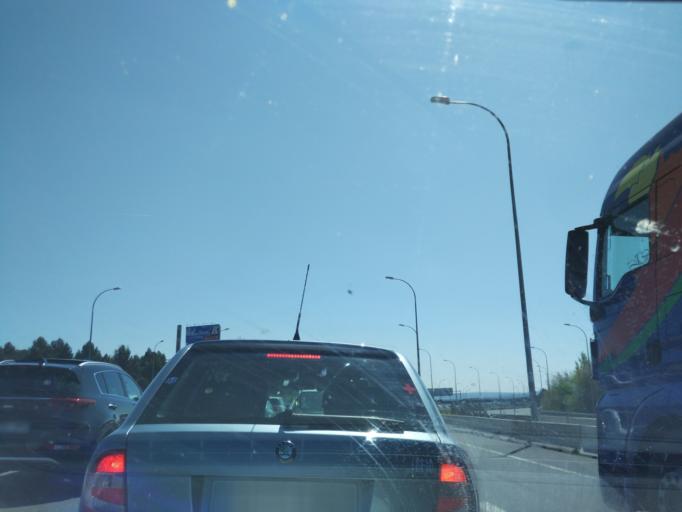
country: ES
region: Madrid
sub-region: Provincia de Madrid
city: Villa de Vallecas
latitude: 40.3570
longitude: -3.5550
